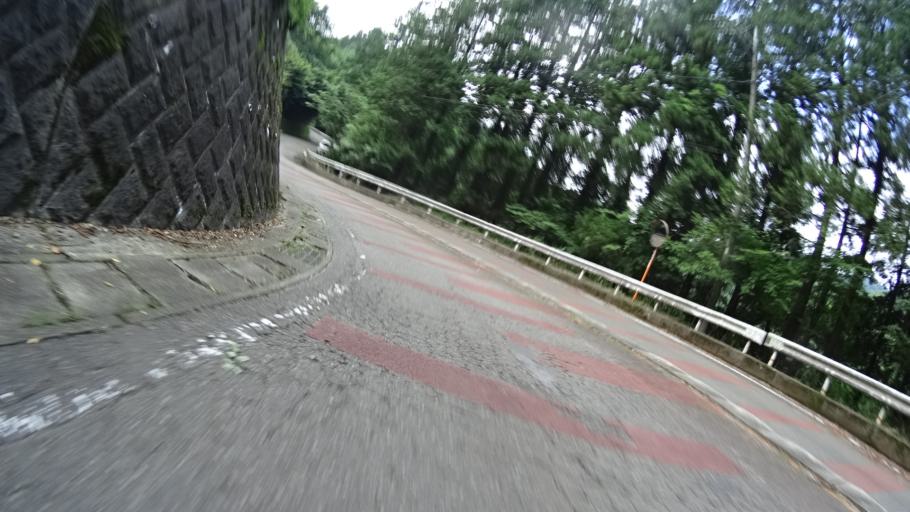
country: JP
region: Kanagawa
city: Hadano
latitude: 35.5006
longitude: 139.2318
